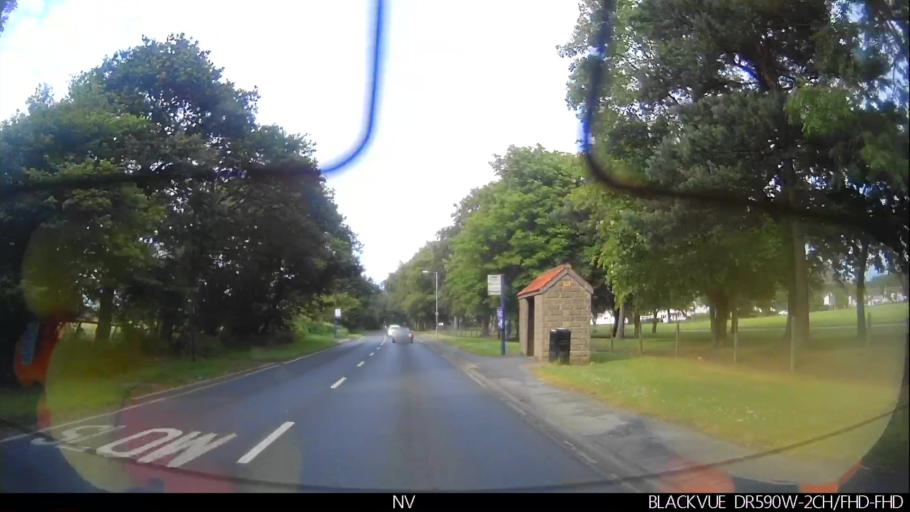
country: GB
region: England
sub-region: North Yorkshire
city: Strensall
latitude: 54.0210
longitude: -1.0449
